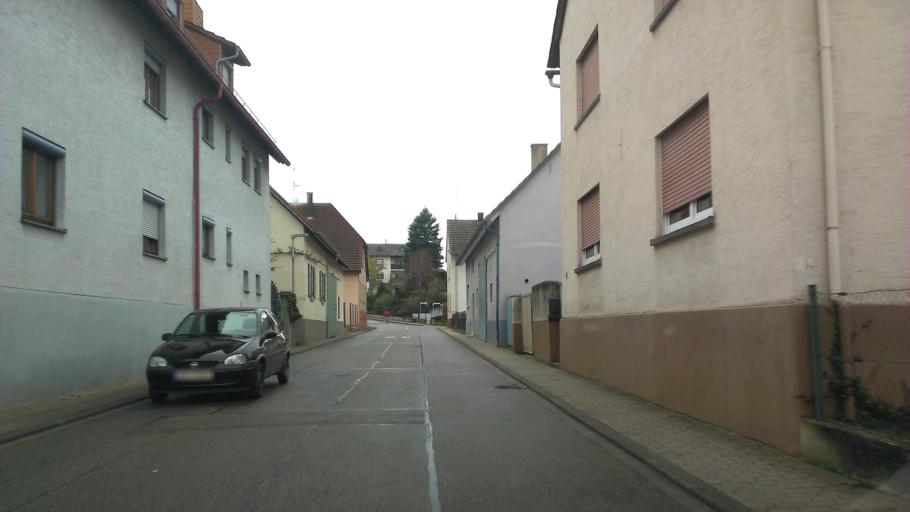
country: DE
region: Baden-Wuerttemberg
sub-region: Karlsruhe Region
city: Zaisenhausen
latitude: 49.1058
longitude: 8.7445
